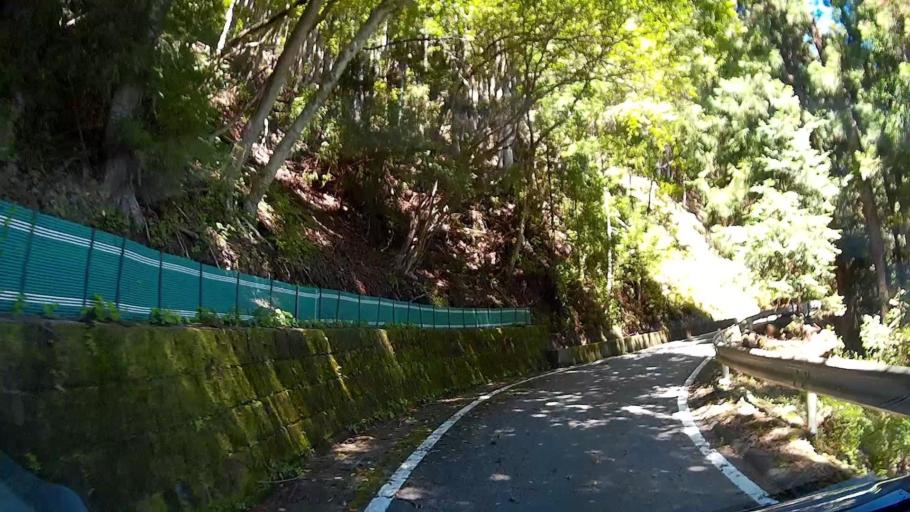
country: JP
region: Shizuoka
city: Shizuoka-shi
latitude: 35.1871
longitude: 138.2631
